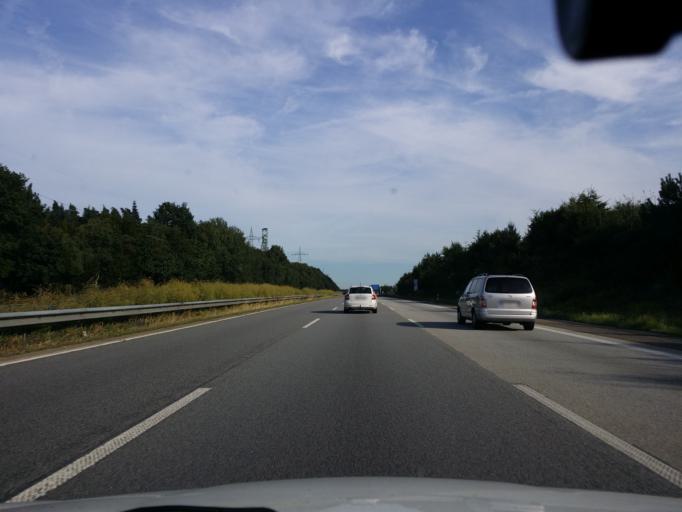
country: DE
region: Rheinland-Pfalz
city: Willroth
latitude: 50.5701
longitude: 7.5142
